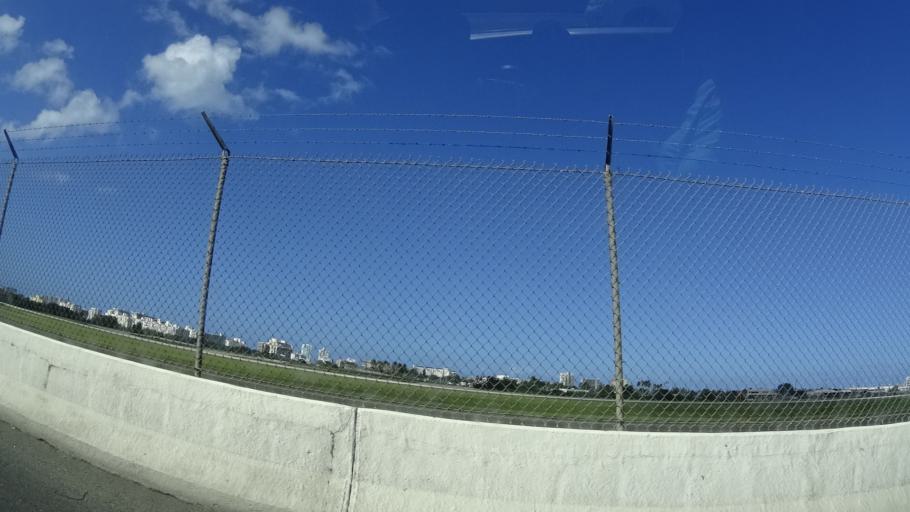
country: PR
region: Carolina
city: Carolina
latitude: 18.4321
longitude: -66.0117
